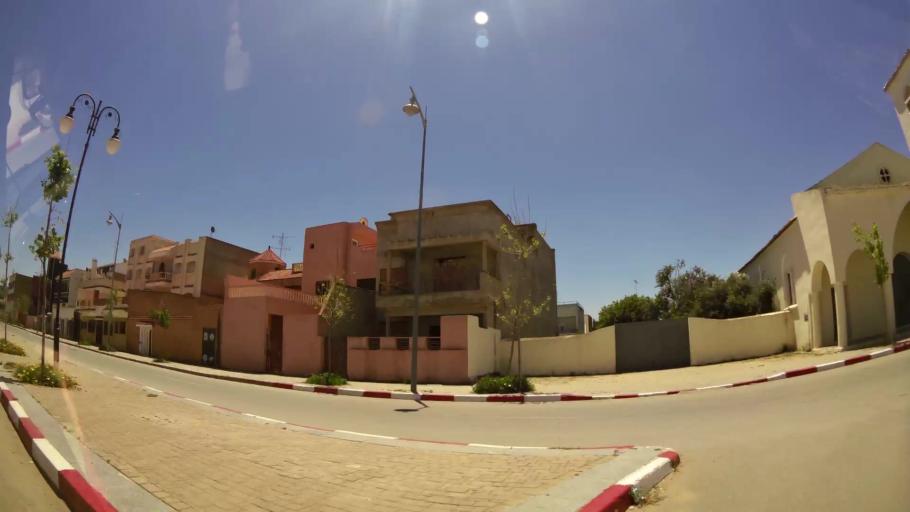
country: MA
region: Oriental
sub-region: Berkane-Taourirt
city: Madagh
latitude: 35.0835
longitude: -2.2229
